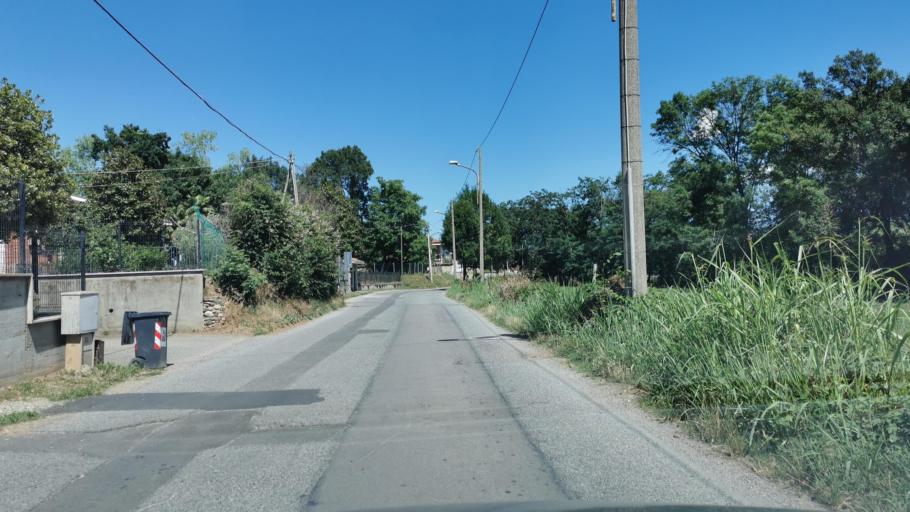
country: IT
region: Piedmont
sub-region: Provincia di Torino
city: Pianezza
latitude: 45.1238
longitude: 7.5460
